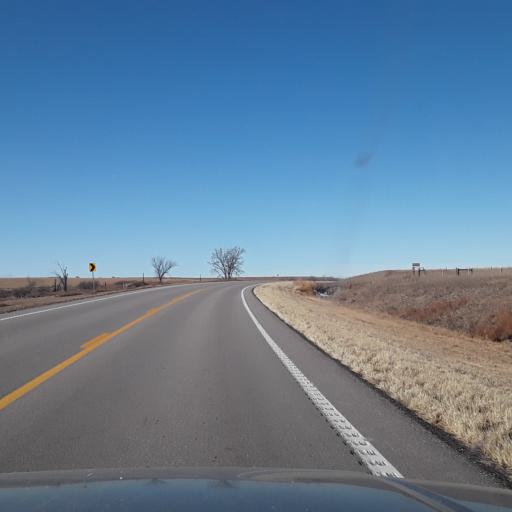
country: US
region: Nebraska
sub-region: Dawson County
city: Cozad
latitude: 40.6804
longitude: -100.1299
